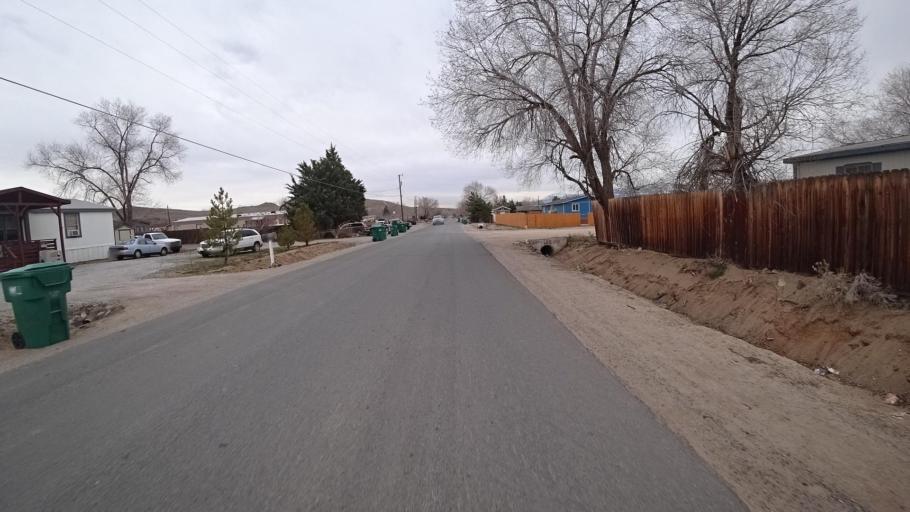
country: US
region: Nevada
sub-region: Washoe County
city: Sun Valley
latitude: 39.5982
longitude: -119.7711
